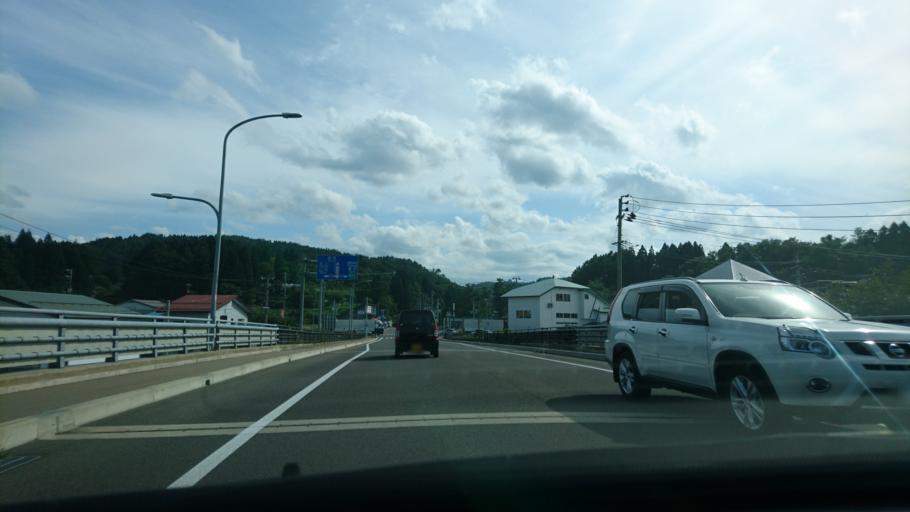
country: JP
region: Akita
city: Yokotemachi
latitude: 39.3067
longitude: 140.5753
